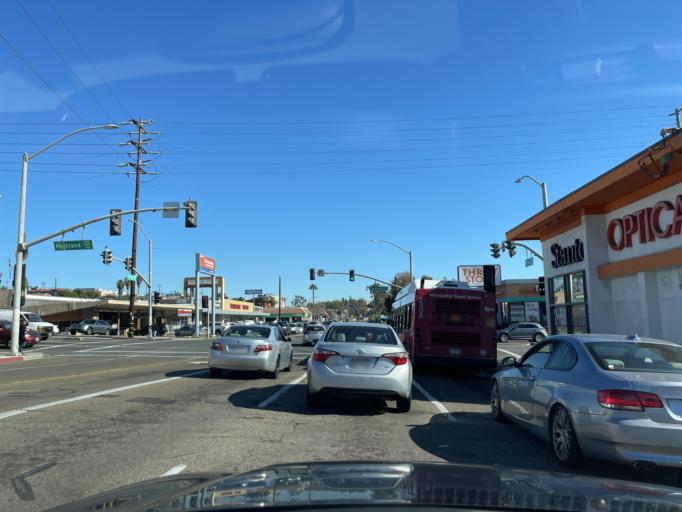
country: US
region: California
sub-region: San Diego County
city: National City
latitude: 32.6763
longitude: -117.0984
